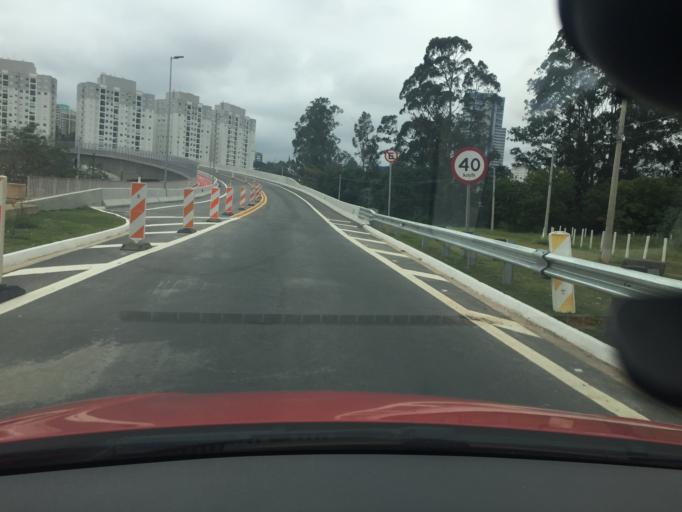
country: BR
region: Sao Paulo
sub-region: Jundiai
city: Jundiai
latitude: -23.1887
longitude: -46.9089
